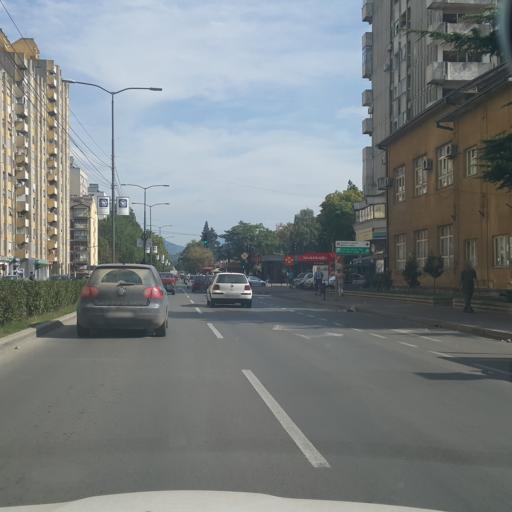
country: RS
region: Central Serbia
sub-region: Nisavski Okrug
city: Nis
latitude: 43.3182
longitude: 21.9103
